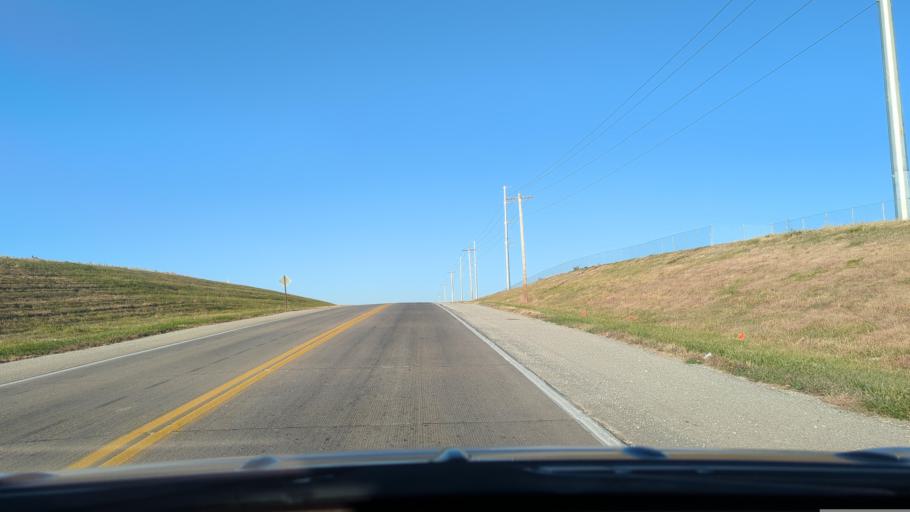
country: US
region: Nebraska
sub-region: Sarpy County
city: Springfield
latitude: 41.1038
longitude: -96.1415
